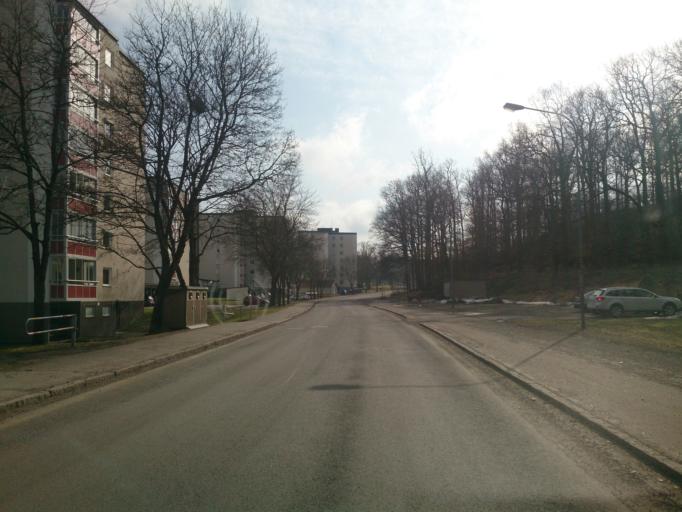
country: SE
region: OEstergoetland
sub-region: Atvidabergs Kommun
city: Atvidaberg
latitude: 58.1941
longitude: 16.0016
